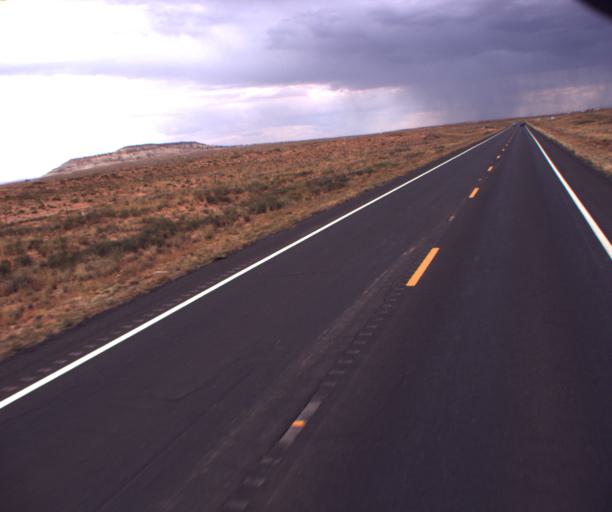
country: US
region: Arizona
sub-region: Coconino County
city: Tuba City
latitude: 36.2775
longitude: -111.0073
